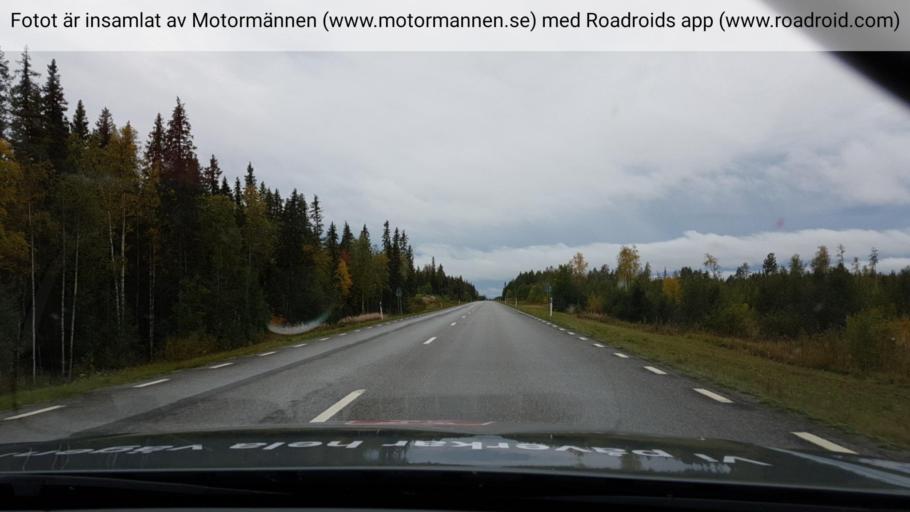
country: SE
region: Jaemtland
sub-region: Stroemsunds Kommun
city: Stroemsund
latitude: 63.7156
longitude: 15.4648
